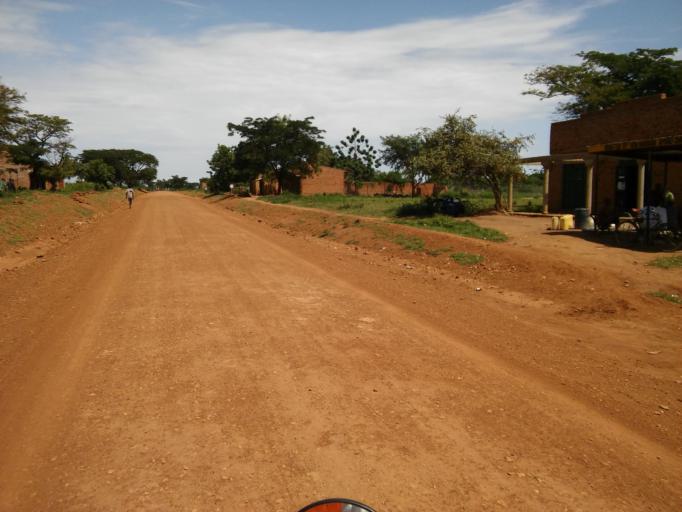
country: UG
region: Eastern Region
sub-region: Kumi District
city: Kumi
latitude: 1.4790
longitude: 33.8897
